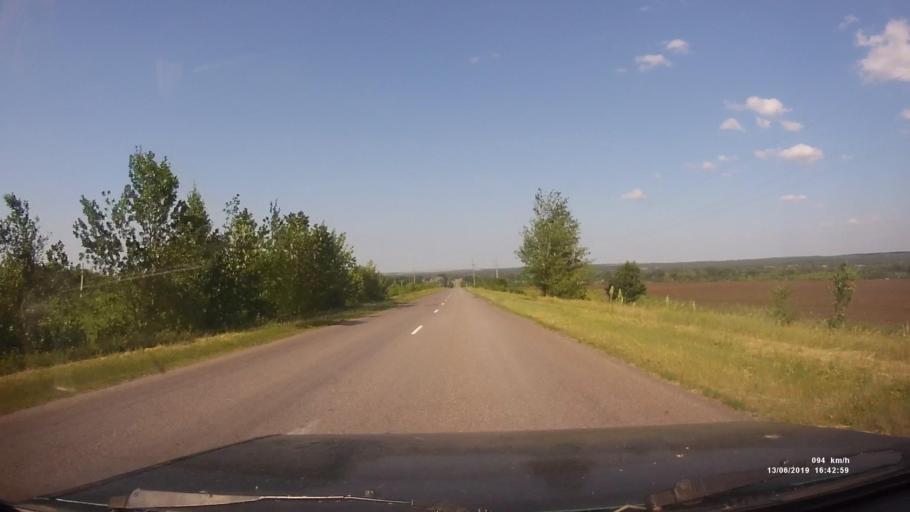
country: RU
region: Rostov
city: Kazanskaya
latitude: 49.9465
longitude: 41.4133
